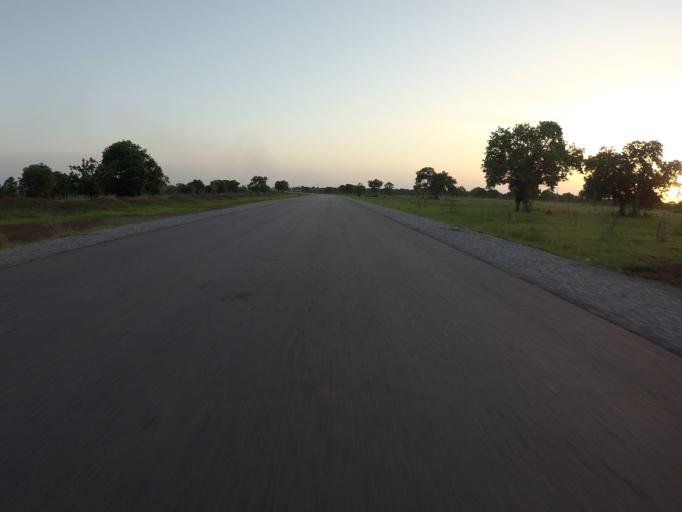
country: GH
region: Northern
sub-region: Yendi
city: Yendi
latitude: 9.9619
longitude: -0.1430
